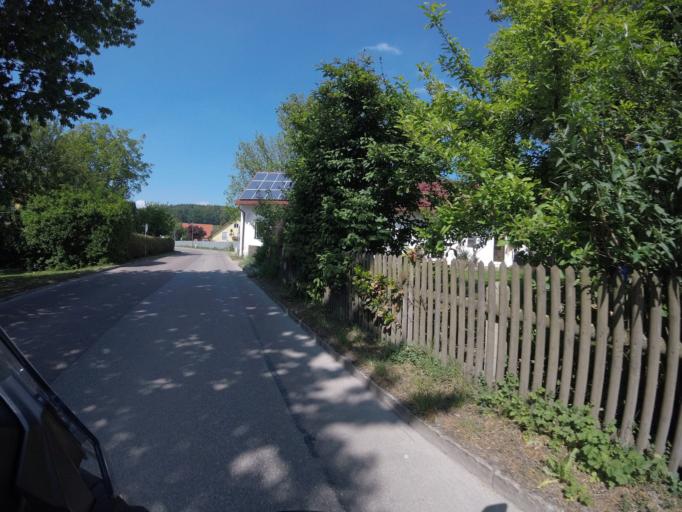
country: DE
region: Bavaria
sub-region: Upper Bavaria
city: Kranzberg
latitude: 48.3836
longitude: 11.6142
